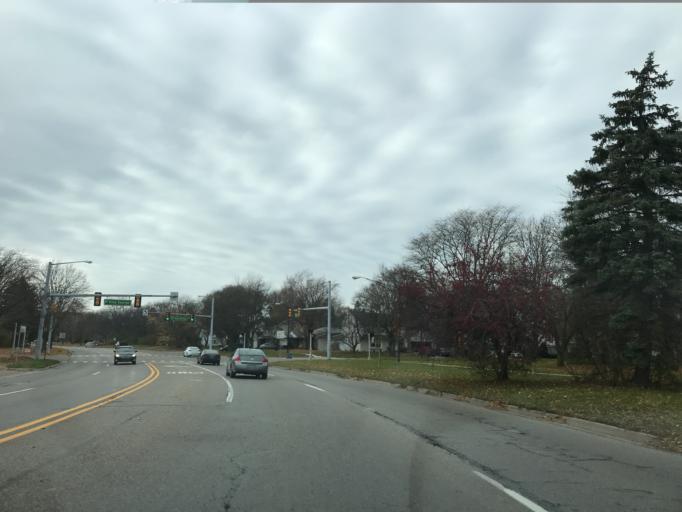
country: US
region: Michigan
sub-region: Washtenaw County
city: Ann Arbor
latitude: 42.2450
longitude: -83.7238
